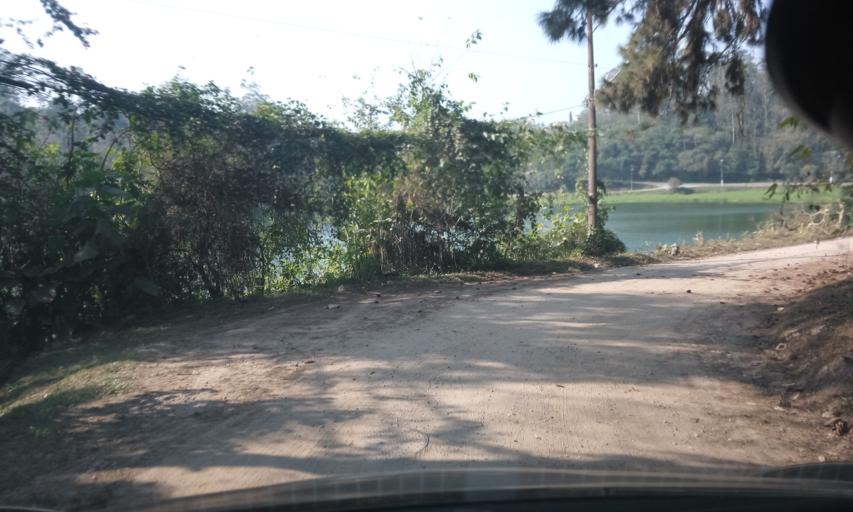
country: BR
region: Sao Paulo
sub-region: Sao Bernardo Do Campo
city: Sao Bernardo do Campo
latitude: -23.7905
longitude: -46.5405
